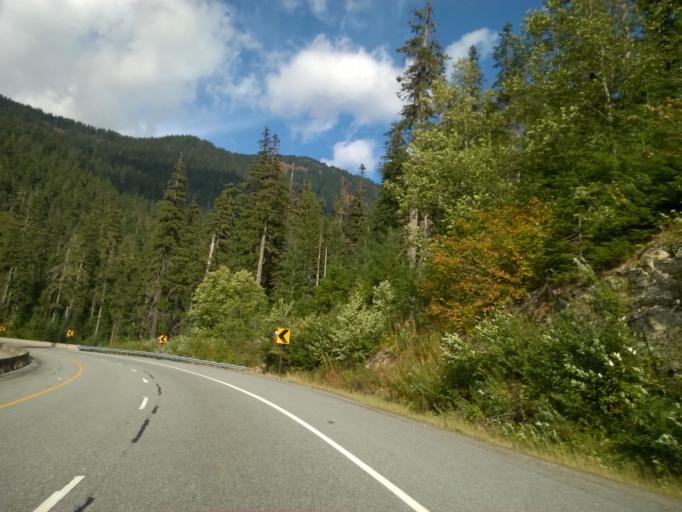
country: US
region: Washington
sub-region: Chelan County
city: Leavenworth
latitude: 47.7176
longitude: -121.1226
